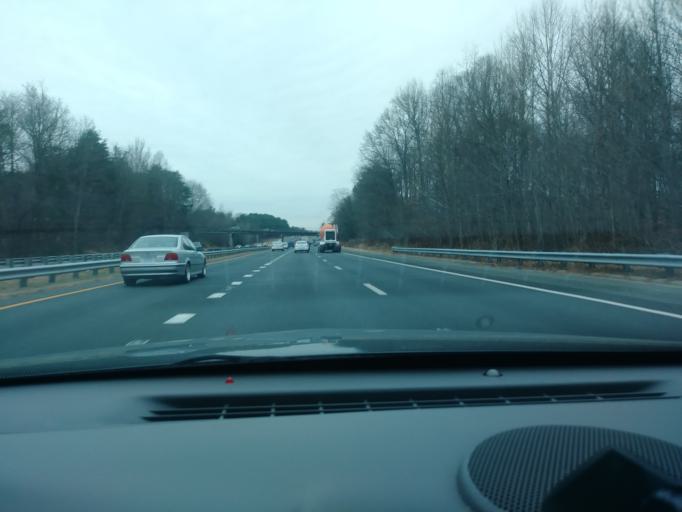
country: US
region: North Carolina
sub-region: Forsyth County
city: Winston-Salem
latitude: 36.0789
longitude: -80.3145
